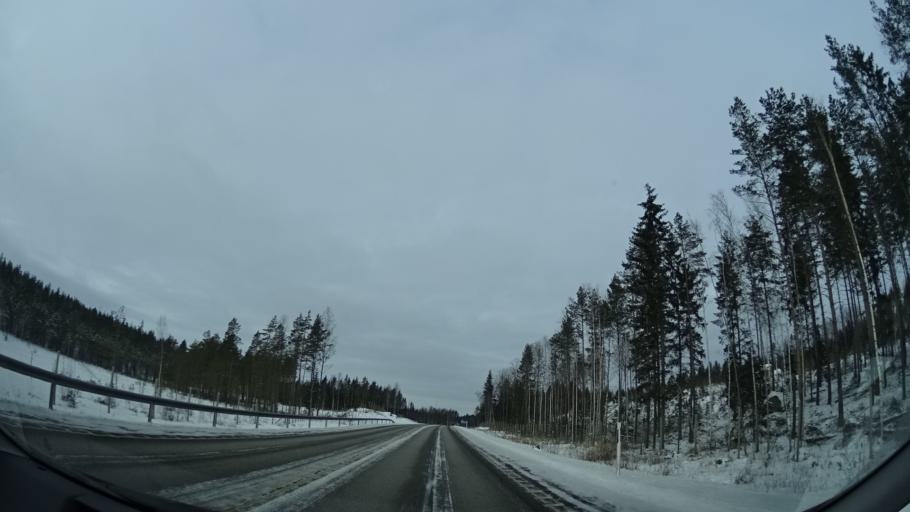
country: FI
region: Uusimaa
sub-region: Helsinki
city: Kaerkoelae
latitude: 60.6108
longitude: 24.0413
